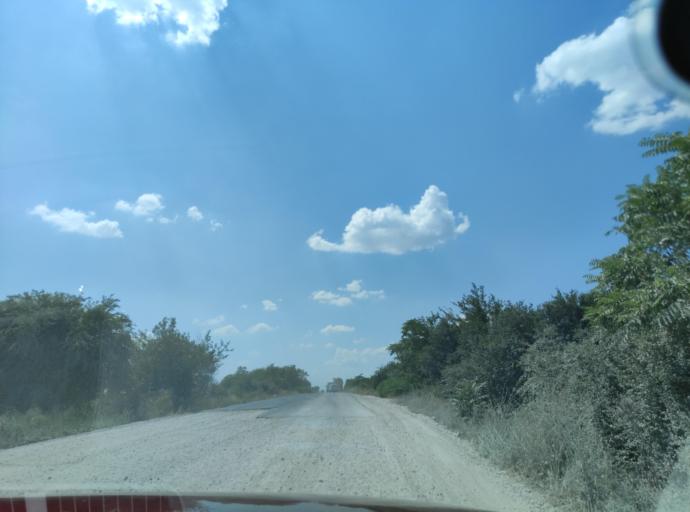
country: BG
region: Pleven
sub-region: Obshtina Knezha
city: Knezha
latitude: 43.4681
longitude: 24.1647
